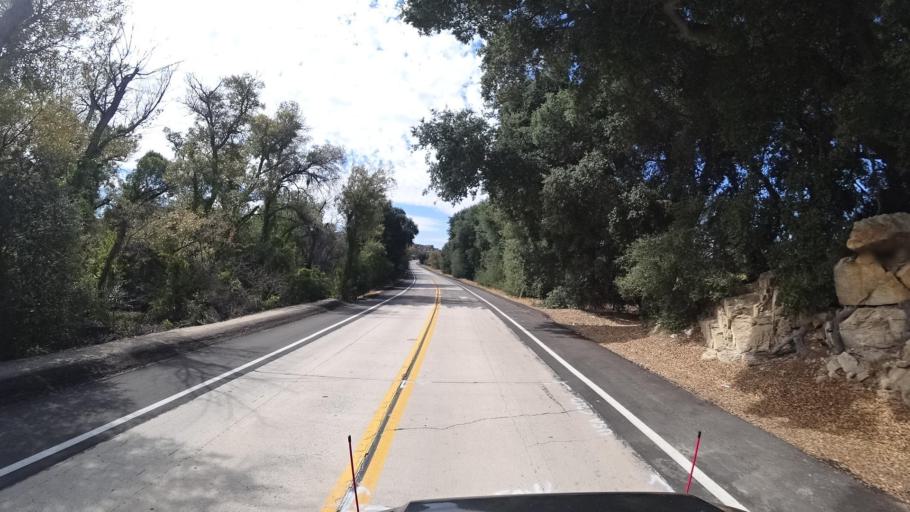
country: MX
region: Baja California
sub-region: Tecate
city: Cereso del Hongo
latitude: 32.6604
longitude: -116.2521
